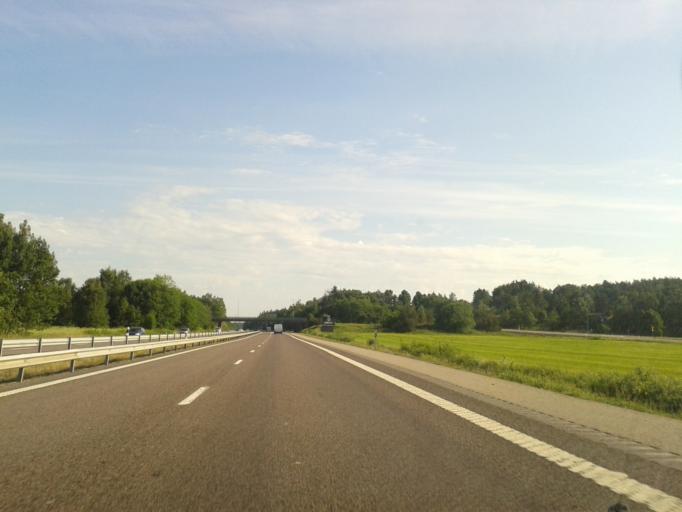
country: SE
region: Vaestra Goetaland
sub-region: Stenungsunds Kommun
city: Stora Hoga
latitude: 57.9824
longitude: 11.8417
